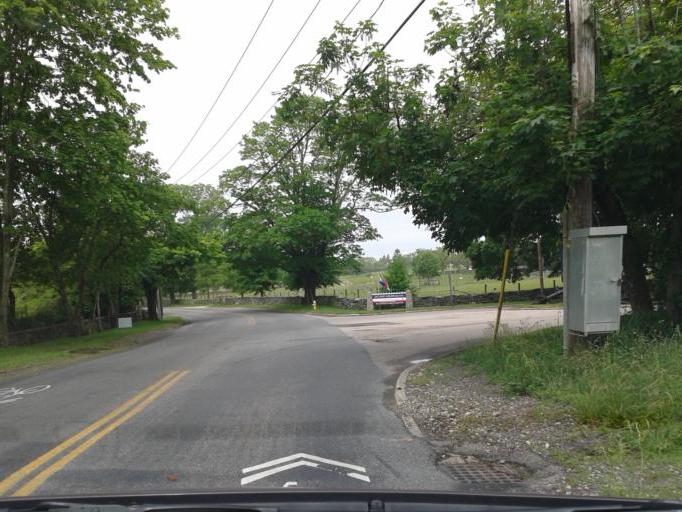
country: US
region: Rhode Island
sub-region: Newport County
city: Newport
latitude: 41.4679
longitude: -71.3397
